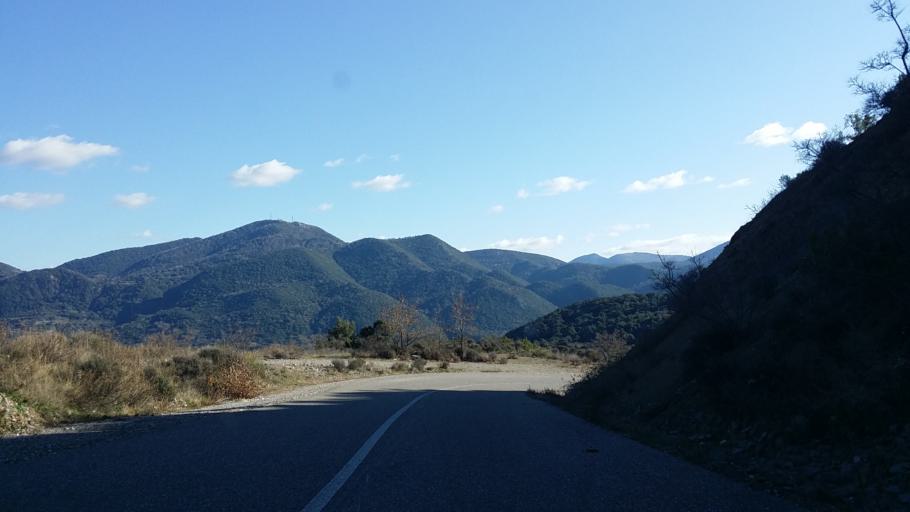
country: GR
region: Central Greece
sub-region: Nomos Evrytanias
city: Kerasochori
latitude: 39.0040
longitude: 21.5400
